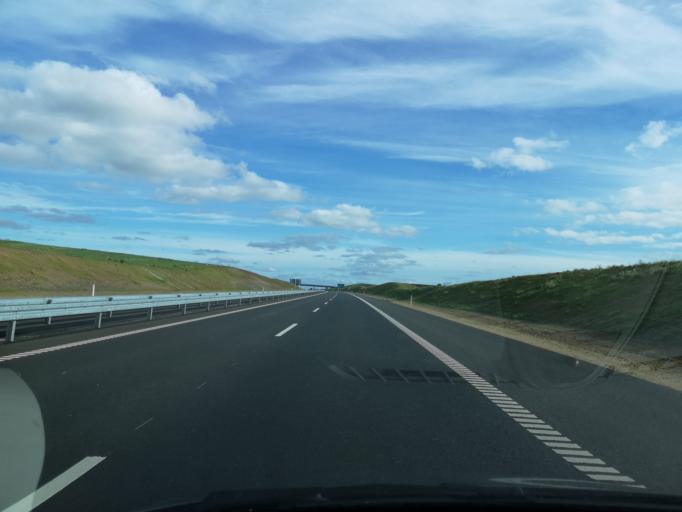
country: DK
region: Central Jutland
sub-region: Holstebro Kommune
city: Holstebro
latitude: 56.3829
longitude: 8.6652
